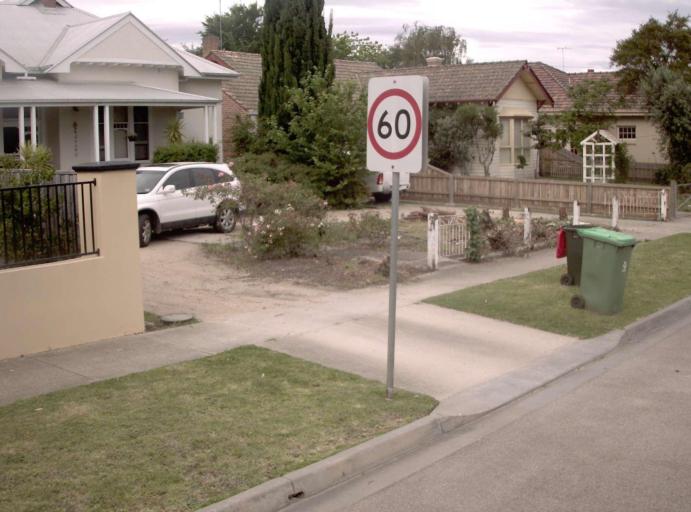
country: AU
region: Victoria
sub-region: East Gippsland
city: Bairnsdale
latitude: -37.8217
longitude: 147.6251
